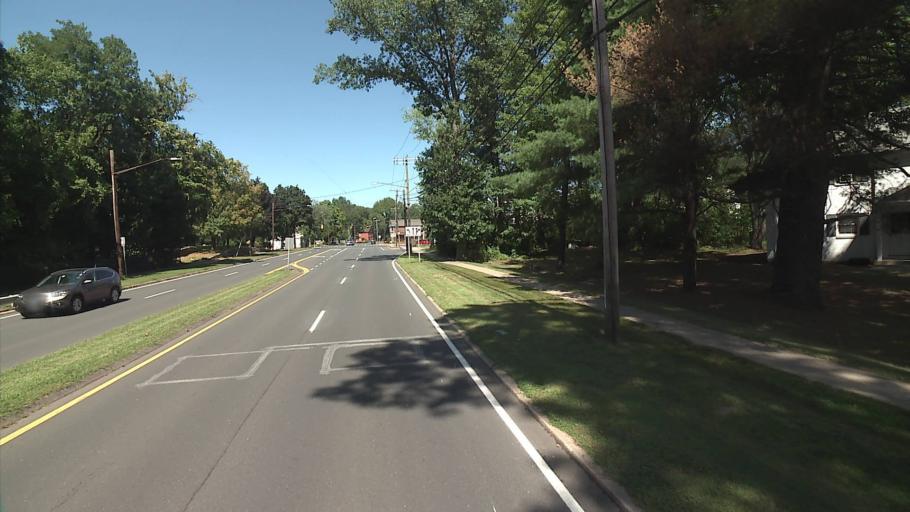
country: US
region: Connecticut
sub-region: Hartford County
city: Windsor
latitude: 41.8280
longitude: -72.6560
